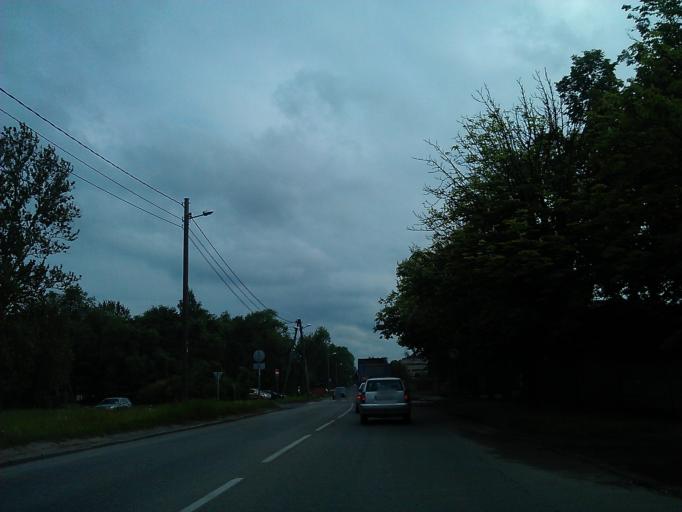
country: LV
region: Riga
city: Riga
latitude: 56.9510
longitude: 24.1628
